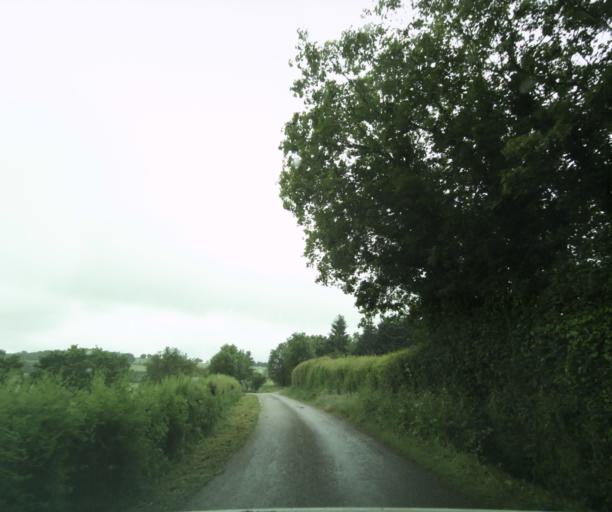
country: FR
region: Bourgogne
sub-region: Departement de Saone-et-Loire
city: Charolles
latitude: 46.4389
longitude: 4.3251
